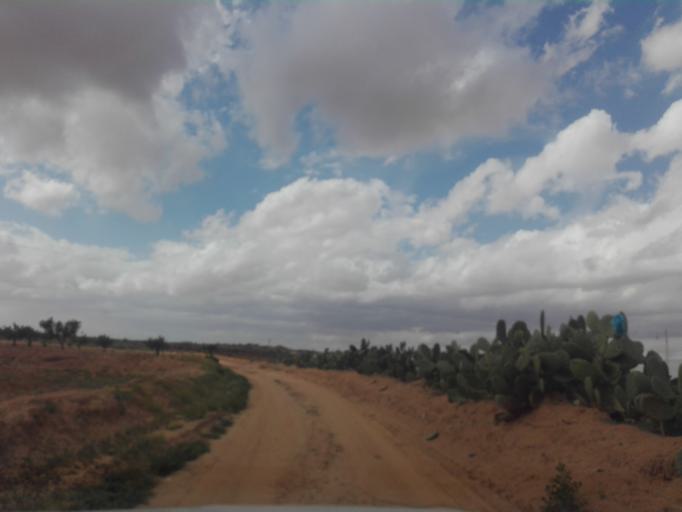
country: TN
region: Safaqis
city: Sfax
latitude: 34.6965
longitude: 10.4451
